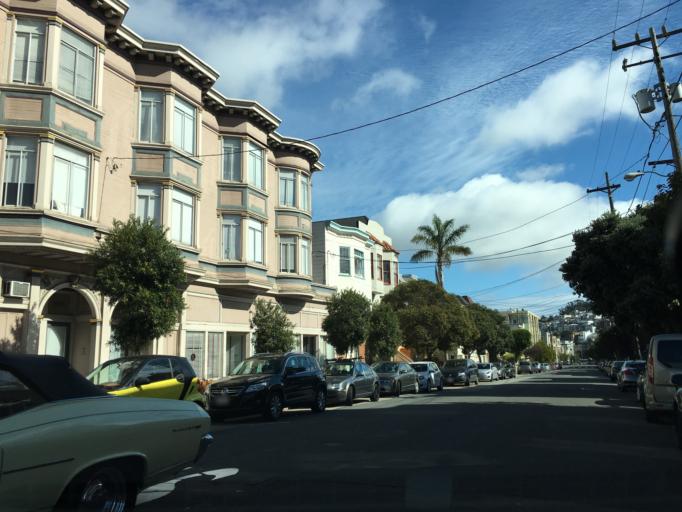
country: US
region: California
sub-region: San Francisco County
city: San Francisco
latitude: 37.7437
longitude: -122.4265
